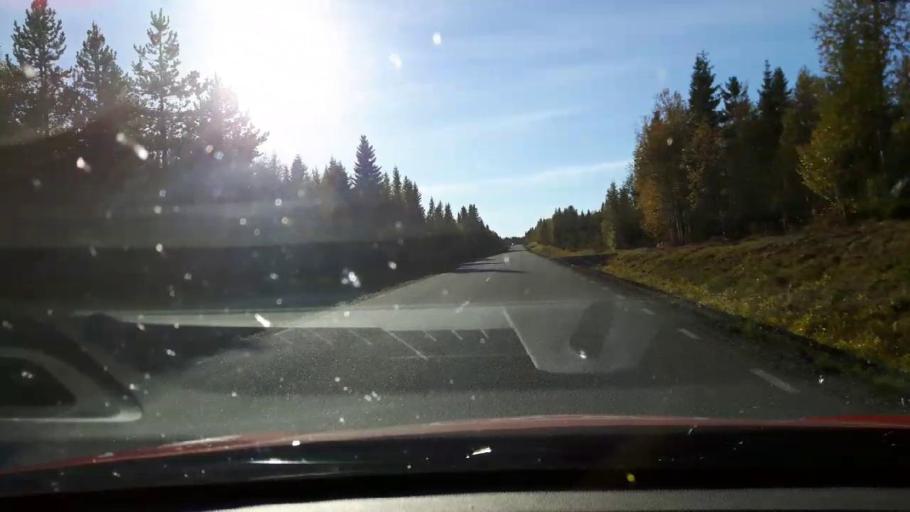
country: SE
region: Jaemtland
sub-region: Stroemsunds Kommun
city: Stroemsund
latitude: 63.8620
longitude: 15.0547
